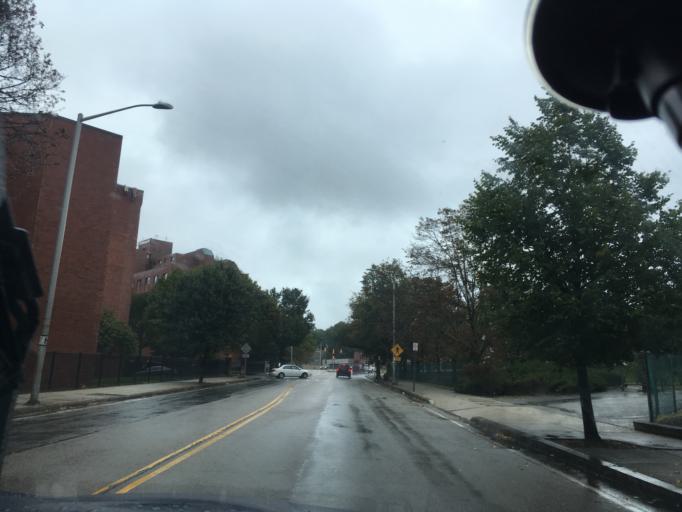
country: US
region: Rhode Island
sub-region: Providence County
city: Providence
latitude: 41.8371
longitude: -71.4110
